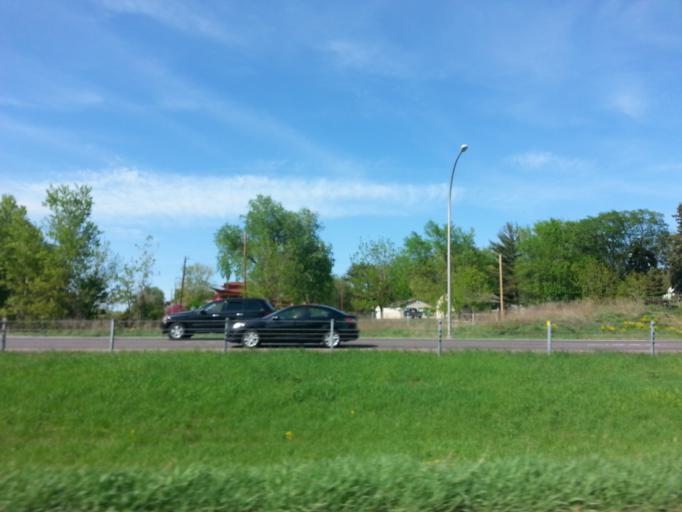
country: US
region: Minnesota
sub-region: Ramsey County
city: Roseville
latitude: 45.0093
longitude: -93.1214
